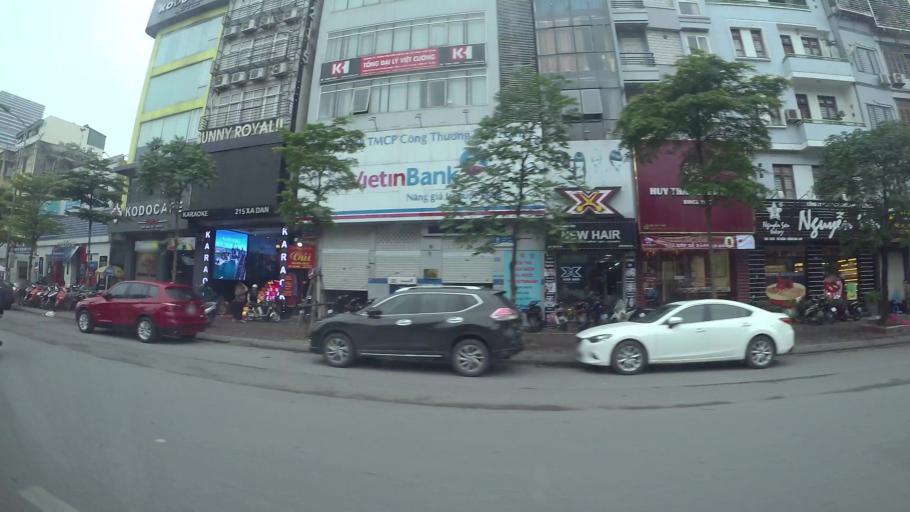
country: VN
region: Ha Noi
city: Dong Da
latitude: 21.0163
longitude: 105.8318
